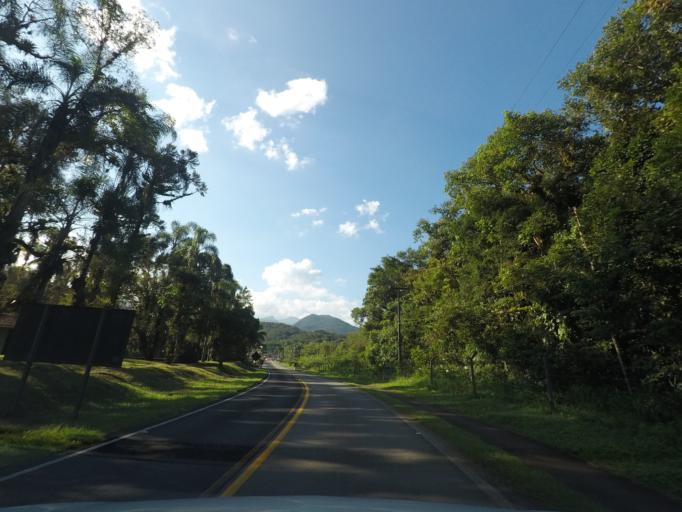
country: BR
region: Parana
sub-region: Antonina
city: Antonina
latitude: -25.3925
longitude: -48.8614
